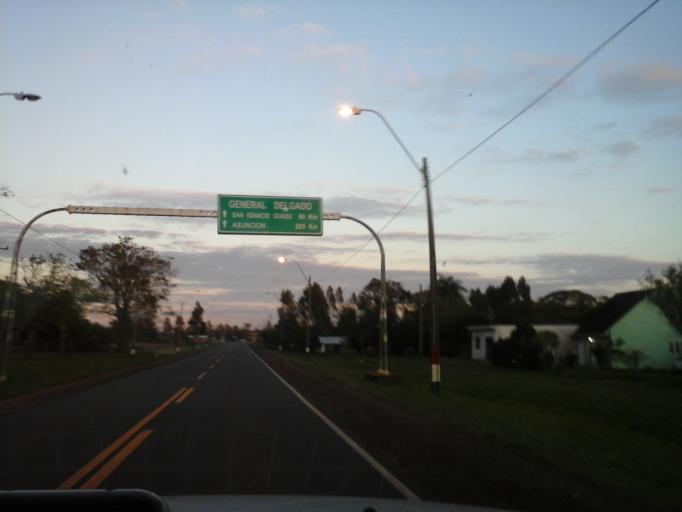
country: PY
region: Itapua
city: General Delgado
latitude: -27.0900
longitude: -56.5151
